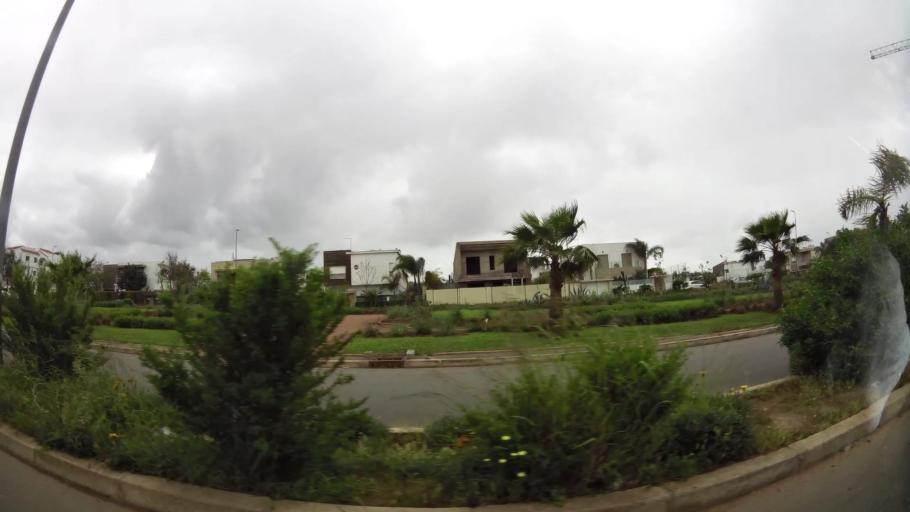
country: MA
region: Grand Casablanca
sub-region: Casablanca
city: Casablanca
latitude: 33.5264
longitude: -7.6143
